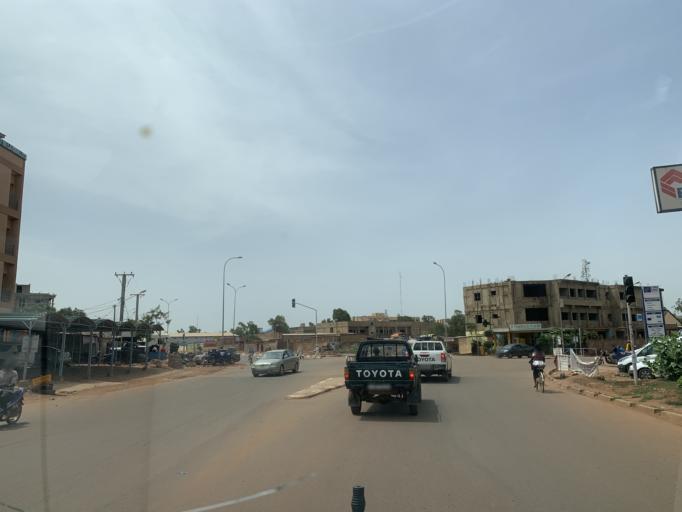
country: BF
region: Centre
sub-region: Kadiogo Province
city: Ouagadougou
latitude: 12.3374
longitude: -1.5084
